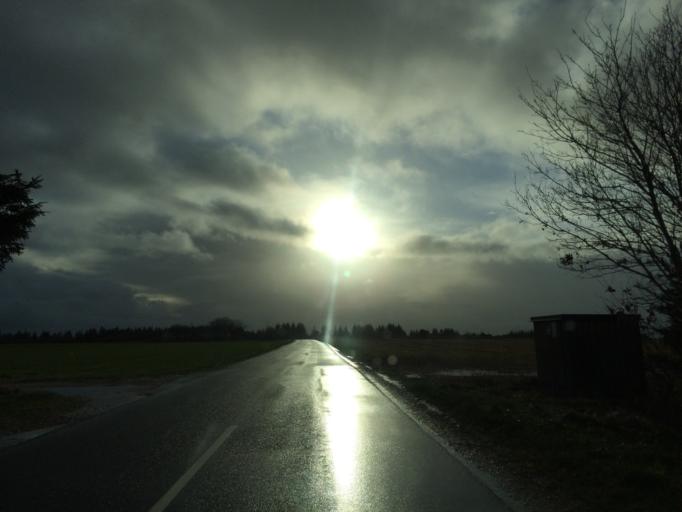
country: DK
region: Central Jutland
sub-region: Holstebro Kommune
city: Ulfborg
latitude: 56.2273
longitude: 8.3839
